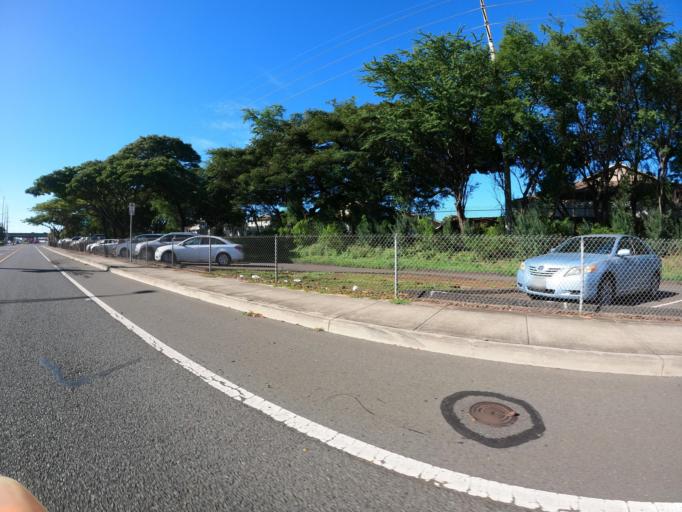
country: US
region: Hawaii
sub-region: Honolulu County
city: Halawa Heights
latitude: 21.3383
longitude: -157.9014
